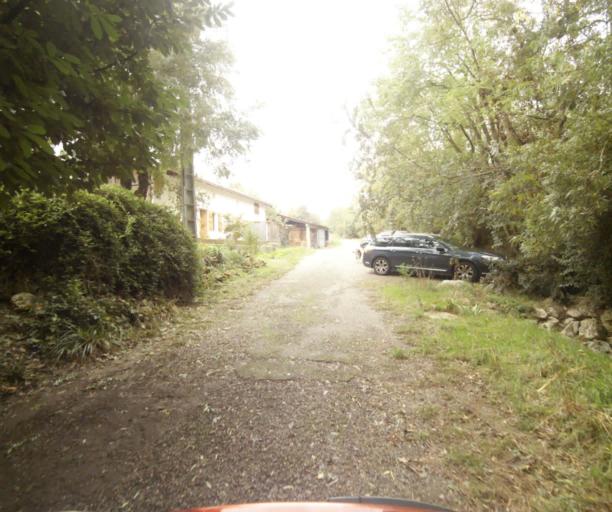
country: FR
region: Midi-Pyrenees
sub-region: Departement du Tarn-et-Garonne
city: Verdun-sur-Garonne
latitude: 43.7985
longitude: 1.2208
